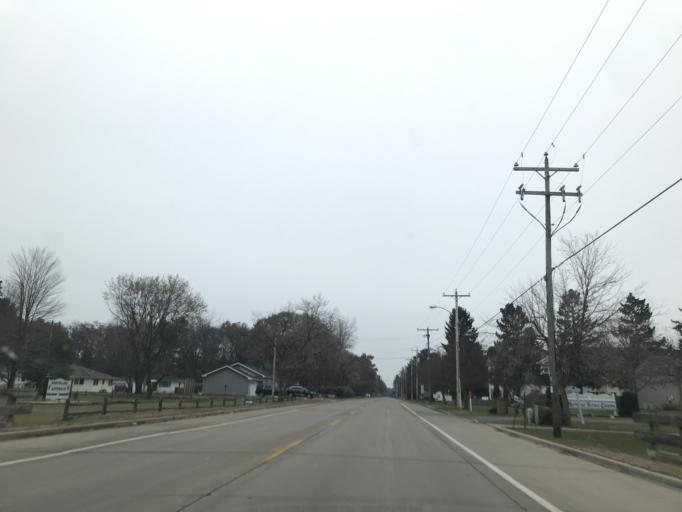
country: US
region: Wisconsin
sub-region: Marinette County
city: Marinette
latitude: 45.0752
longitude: -87.6194
